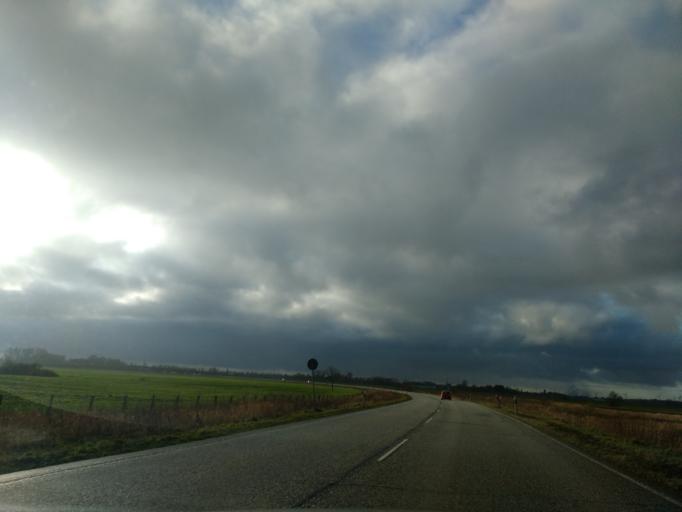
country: DE
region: Schleswig-Holstein
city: Bekdorf
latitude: 53.9319
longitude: 9.4139
